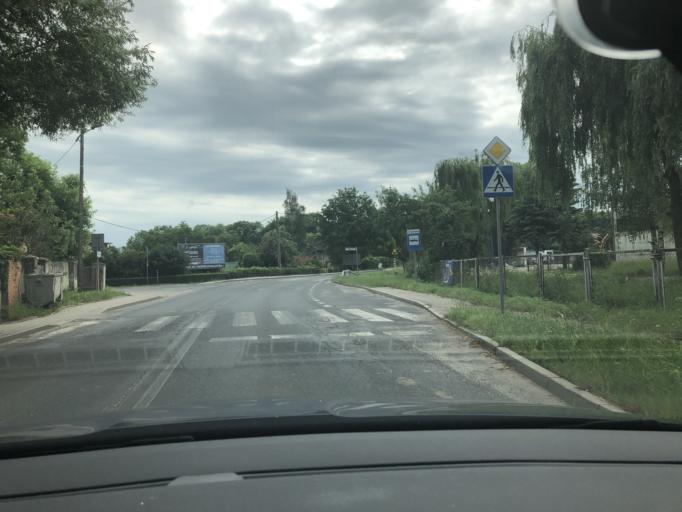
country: PL
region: Lower Silesian Voivodeship
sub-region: Powiat zlotoryjski
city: Zlotoryja
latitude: 51.1369
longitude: 15.9243
